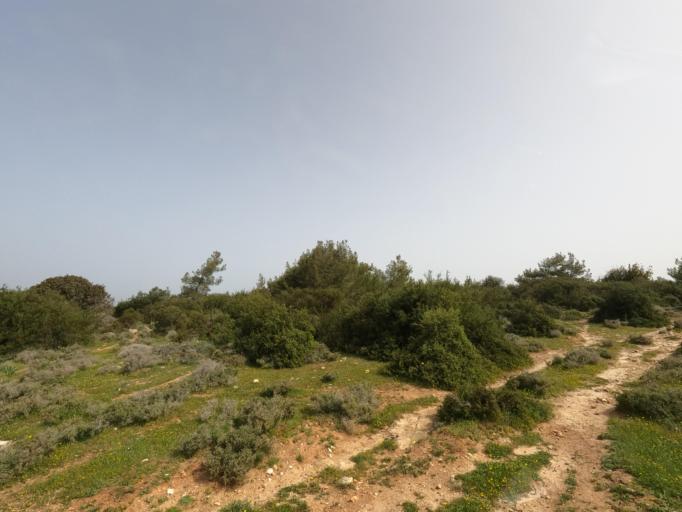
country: CY
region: Pafos
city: Polis
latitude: 35.0130
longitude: 32.3686
